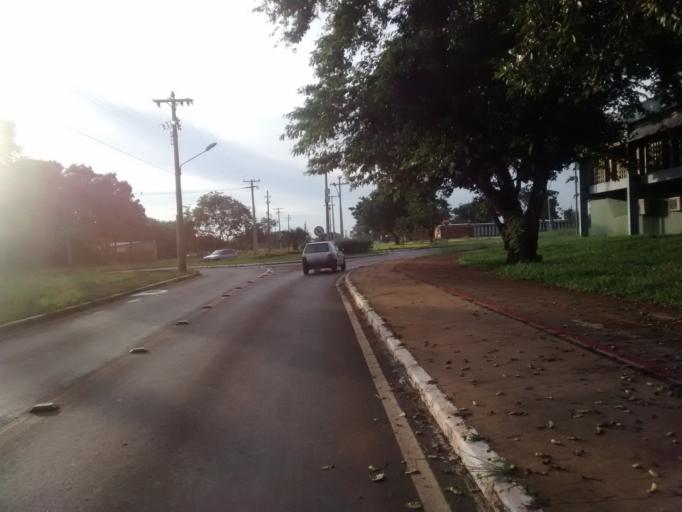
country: BR
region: Federal District
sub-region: Brasilia
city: Brasilia
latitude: -15.7678
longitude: -47.8686
